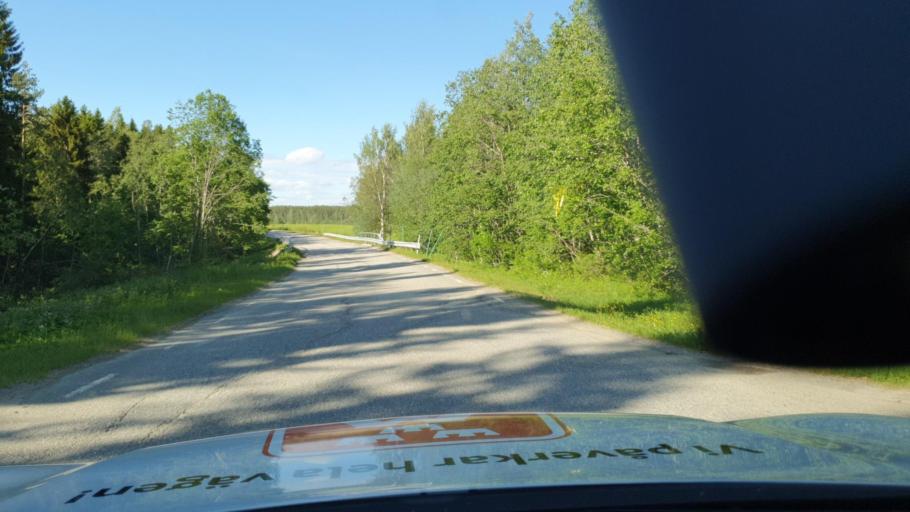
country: SE
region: Vaesterbotten
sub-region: Vannas Kommun
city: Vaennaes
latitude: 63.8488
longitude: 19.6237
